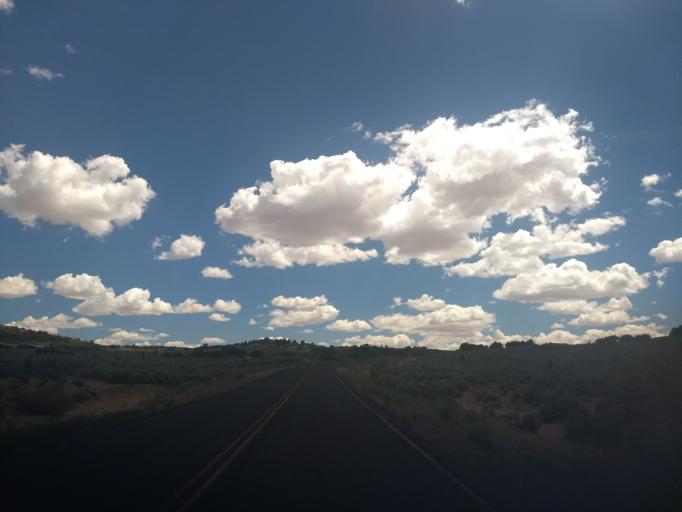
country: US
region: Utah
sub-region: Kane County
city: Kanab
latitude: 37.1319
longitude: -112.6763
